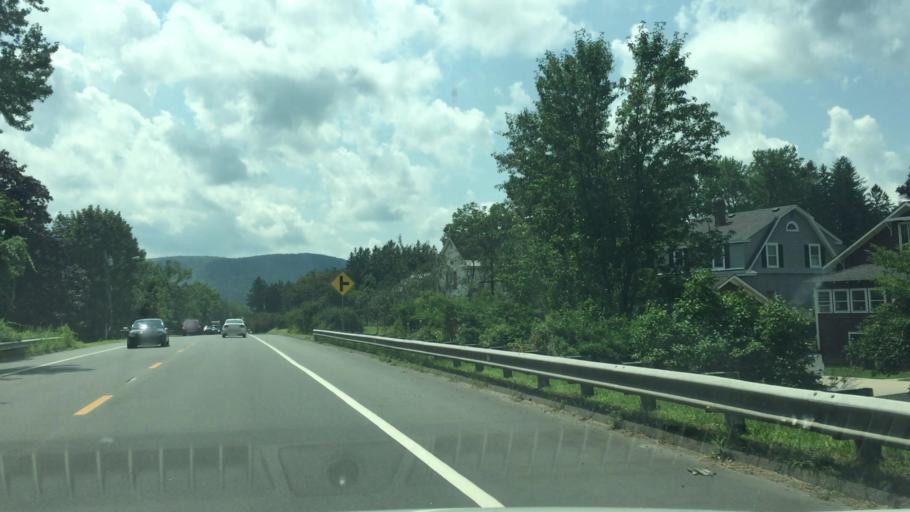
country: US
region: Massachusetts
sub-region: Berkshire County
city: Lee
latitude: 42.2918
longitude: -73.2413
